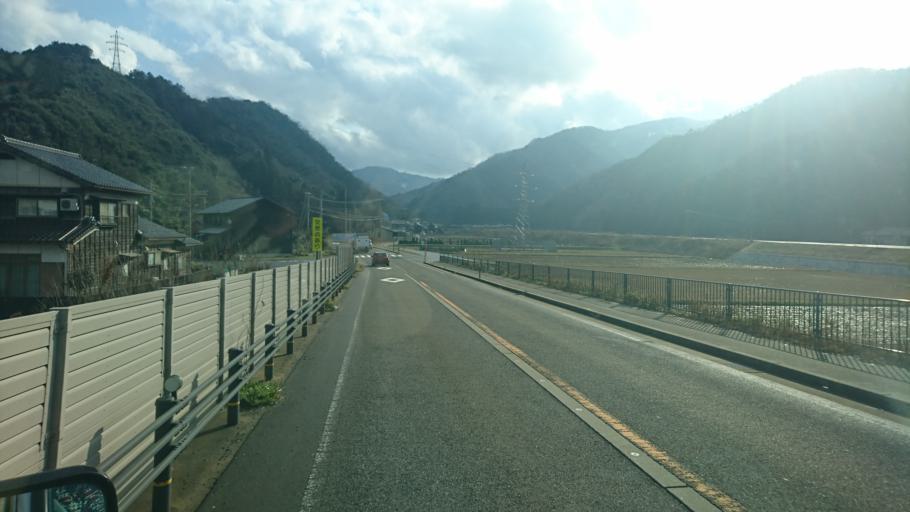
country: JP
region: Tottori
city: Tottori
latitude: 35.6074
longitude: 134.4703
